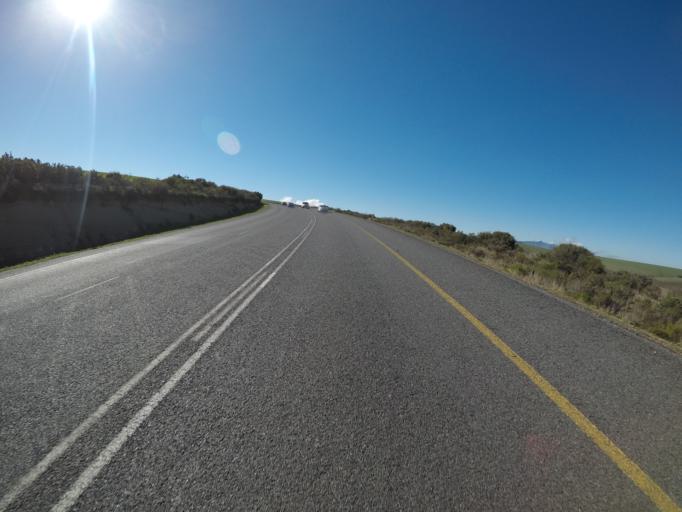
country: ZA
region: Western Cape
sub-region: Overberg District Municipality
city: Caledon
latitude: -34.2284
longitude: 19.2720
